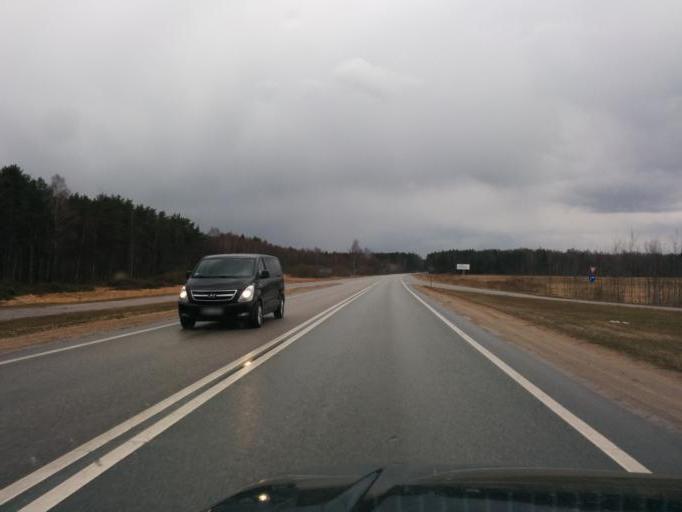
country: LV
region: Marupe
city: Marupe
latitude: 56.8380
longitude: 24.0301
